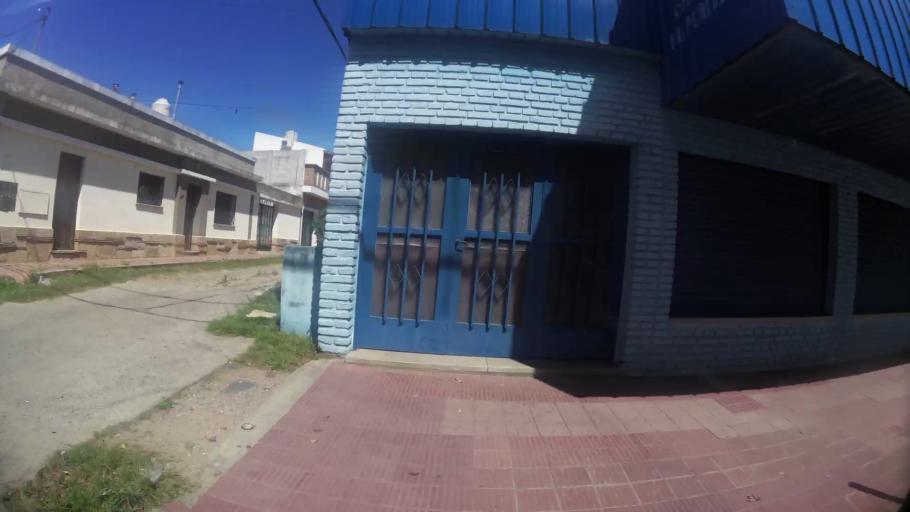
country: AR
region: Cordoba
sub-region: Departamento de Capital
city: Cordoba
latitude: -31.4173
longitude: -64.2160
